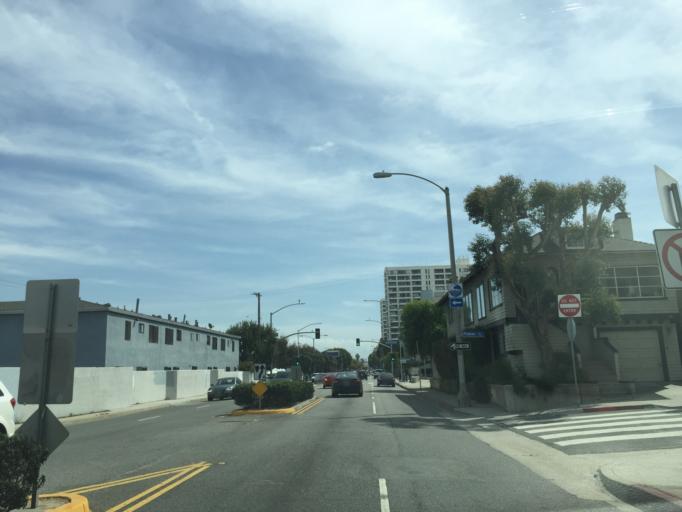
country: US
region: California
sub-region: Los Angeles County
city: Santa Monica
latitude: 34.0025
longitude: -118.4852
